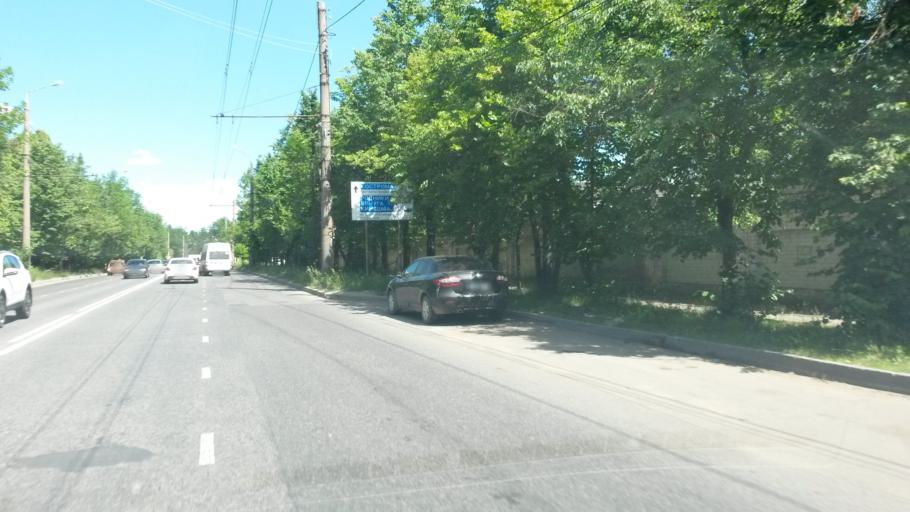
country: RU
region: Ivanovo
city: Kokhma
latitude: 56.9691
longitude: 41.0500
